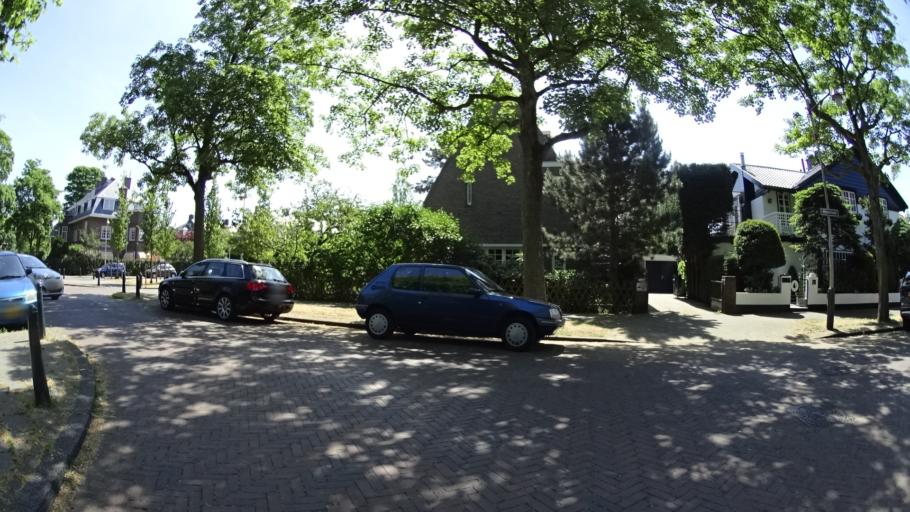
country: NL
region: South Holland
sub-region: Gemeente Den Haag
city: Scheveningen
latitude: 52.0835
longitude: 4.2641
